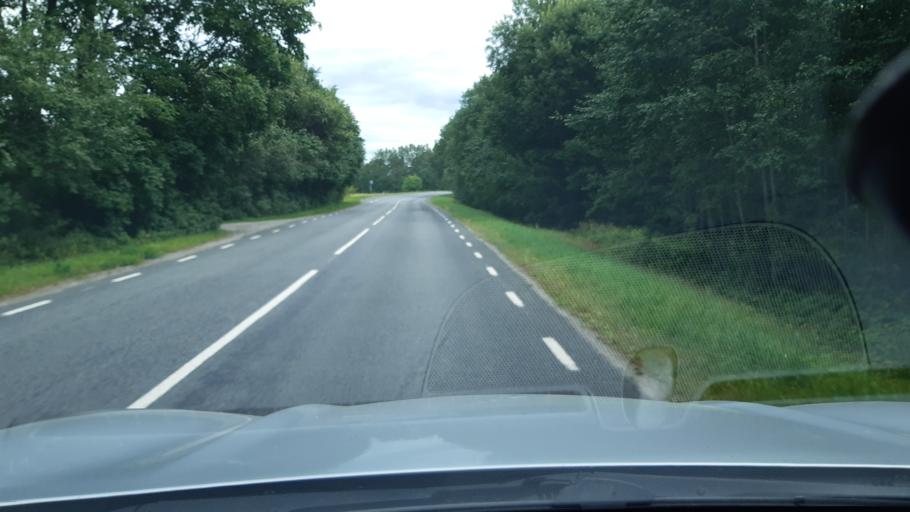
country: EE
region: Raplamaa
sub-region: Maerjamaa vald
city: Marjamaa
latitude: 59.0459
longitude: 24.4763
